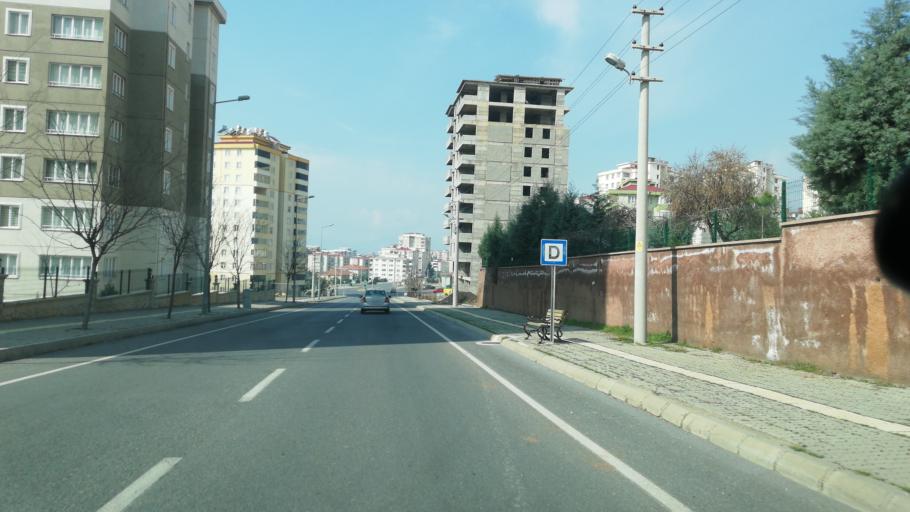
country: TR
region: Kahramanmaras
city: Kahramanmaras
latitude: 37.5867
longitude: 36.8720
